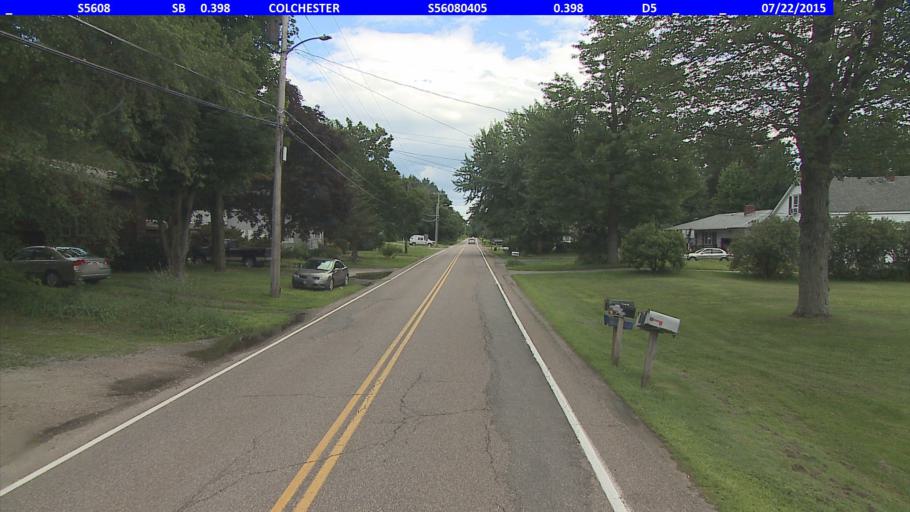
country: US
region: Vermont
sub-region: Chittenden County
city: Winooski
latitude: 44.5048
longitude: -73.2004
